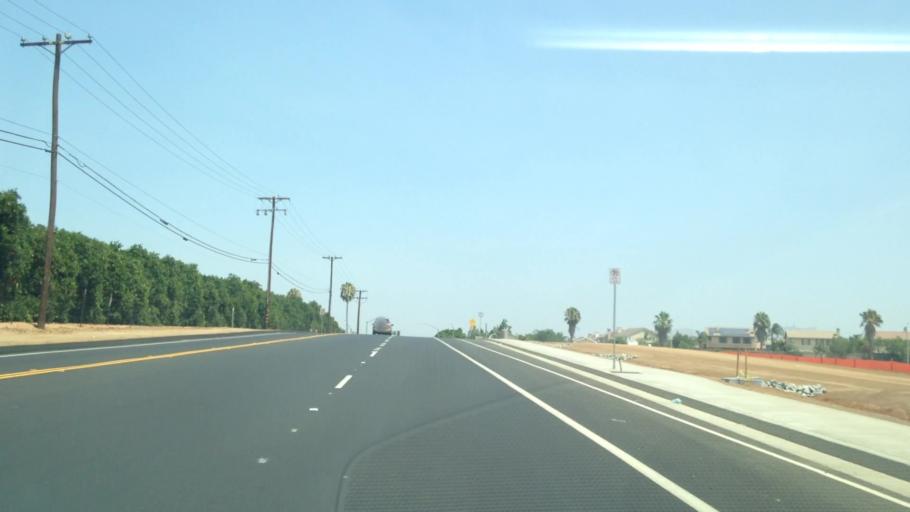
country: US
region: California
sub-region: Riverside County
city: Woodcrest
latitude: 33.8860
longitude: -117.3139
